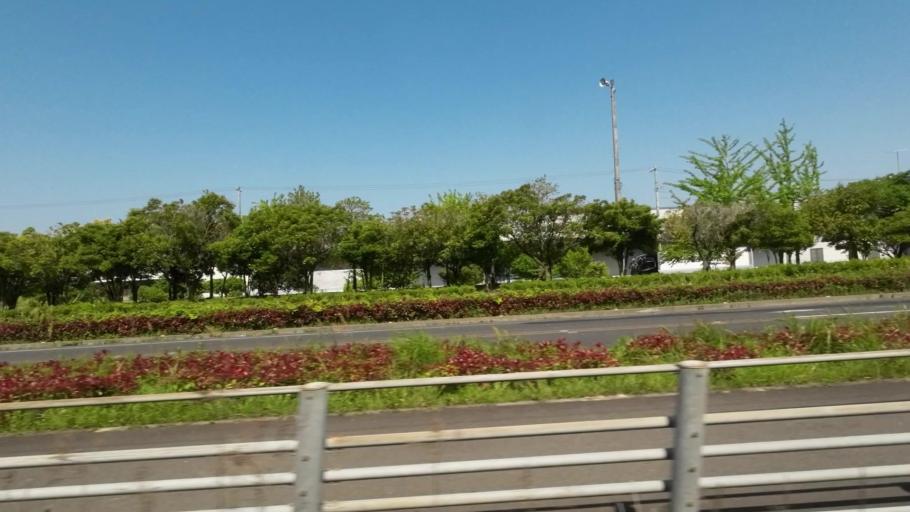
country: JP
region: Ehime
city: Kawanoecho
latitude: 34.0264
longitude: 133.5819
